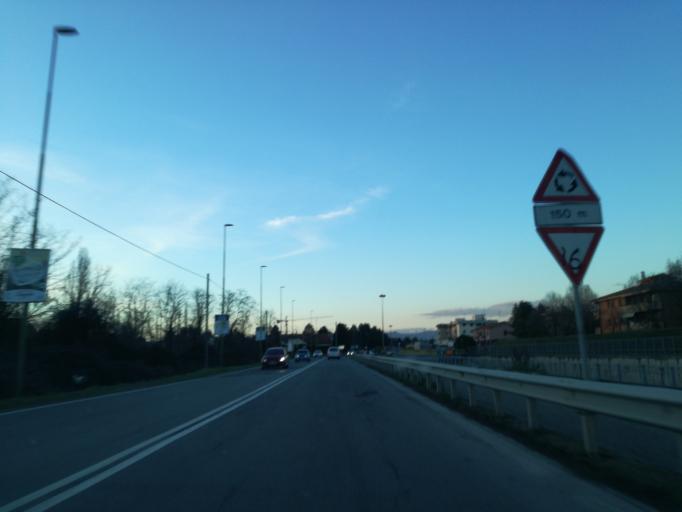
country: IT
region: Lombardy
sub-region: Provincia di Monza e Brianza
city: Vimercate
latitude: 45.6102
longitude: 9.3600
